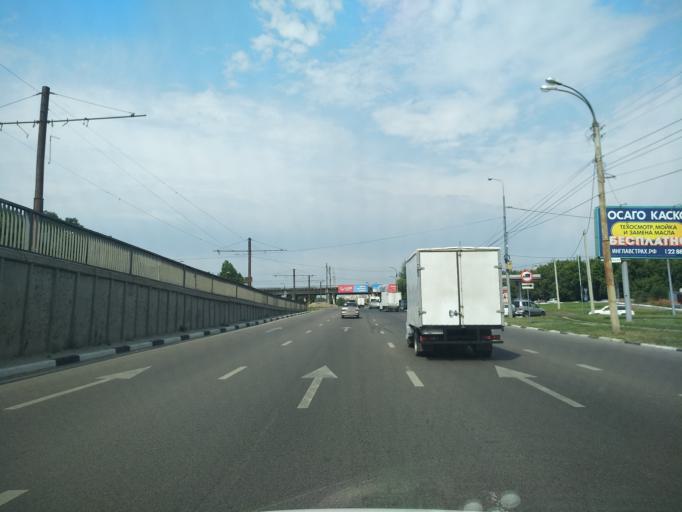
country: RU
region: Voronezj
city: Voronezh
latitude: 51.6941
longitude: 39.2315
